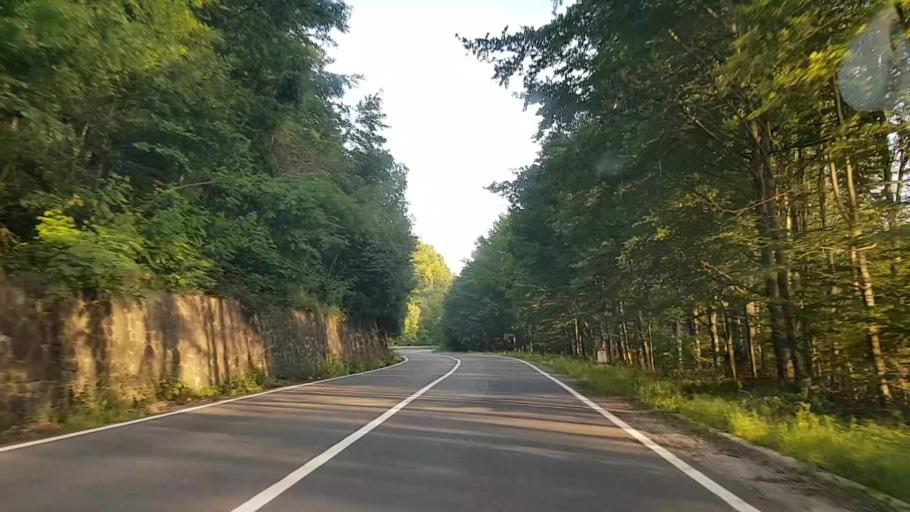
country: RO
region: Harghita
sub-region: Comuna Corund
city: Corund
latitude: 46.4461
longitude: 25.2282
